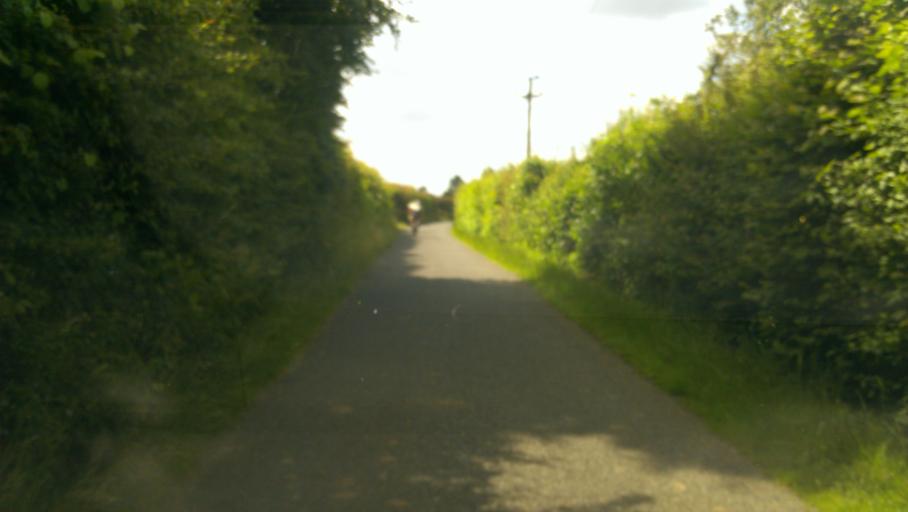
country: GB
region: England
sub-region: Essex
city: Rayne
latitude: 51.8594
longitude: 0.6305
